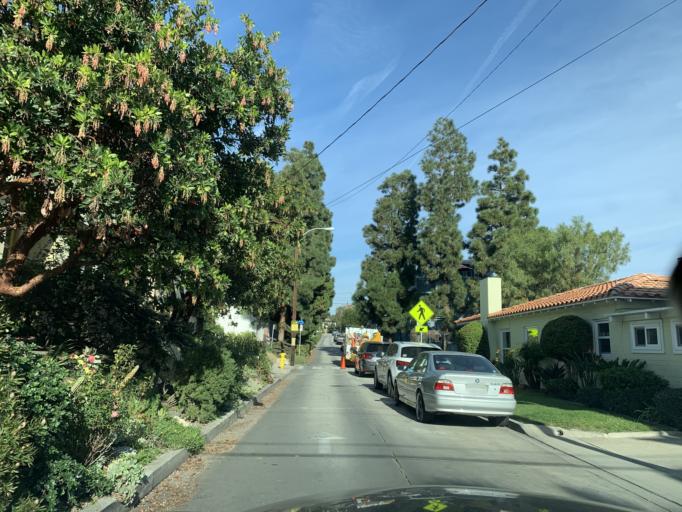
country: US
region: California
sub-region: Los Angeles County
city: Manhattan Beach
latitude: 33.8811
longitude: -118.4051
